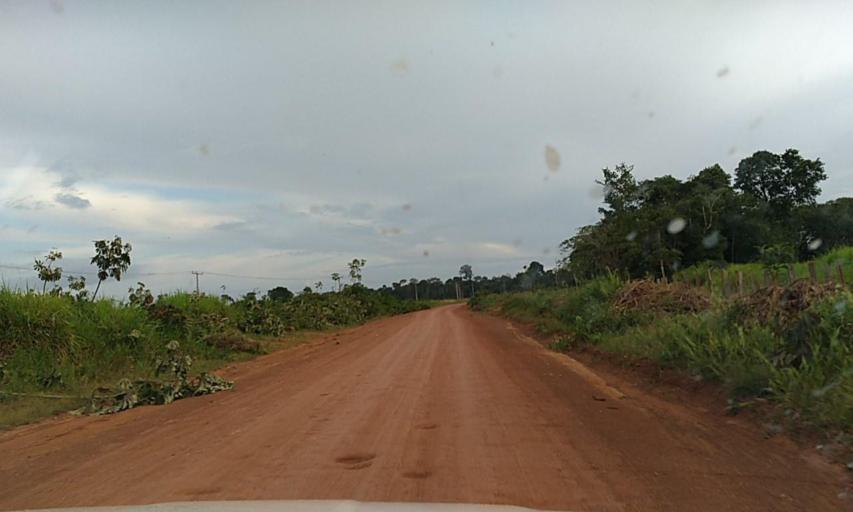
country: BR
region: Para
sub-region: Senador Jose Porfirio
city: Senador Jose Porfirio
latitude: -2.6947
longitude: -51.8234
